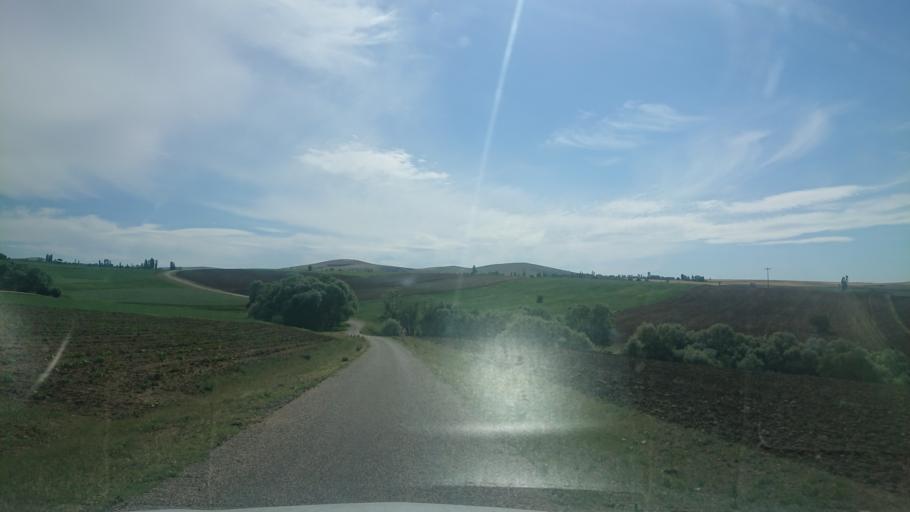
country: TR
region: Aksaray
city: Ortakoy
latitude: 38.8157
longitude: 33.9988
